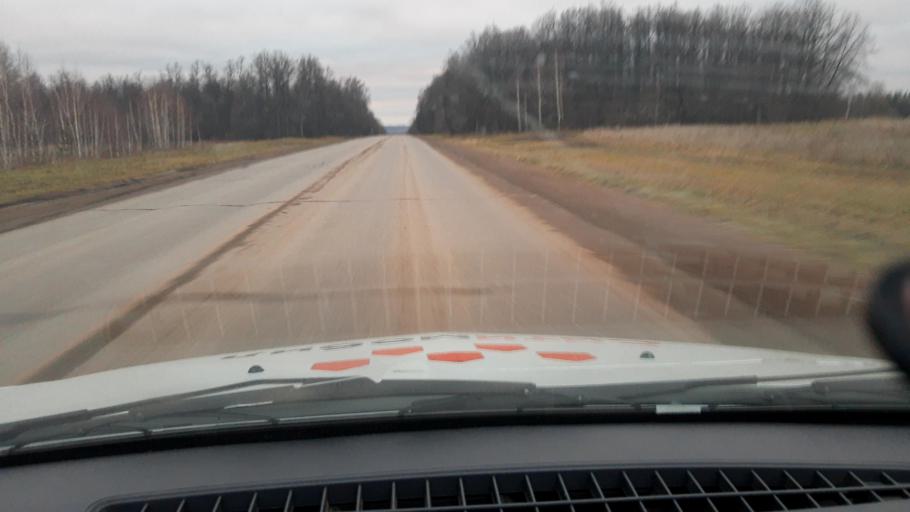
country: RU
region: Bashkortostan
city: Iglino
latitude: 54.7761
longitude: 56.4157
